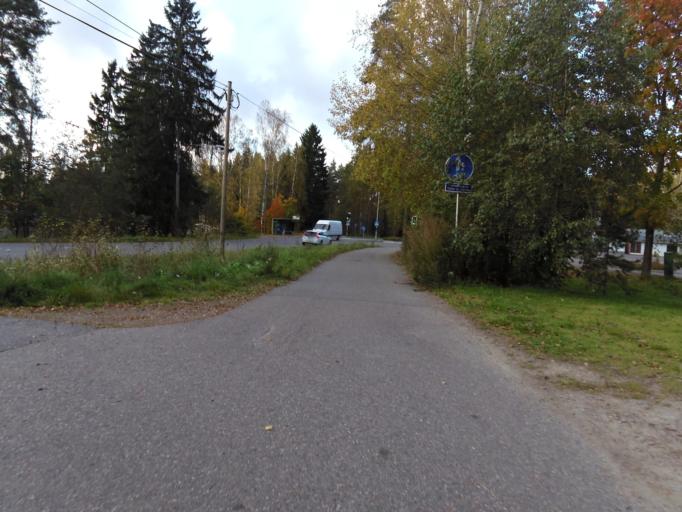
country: FI
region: Uusimaa
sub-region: Helsinki
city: Kauniainen
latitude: 60.2829
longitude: 24.7464
